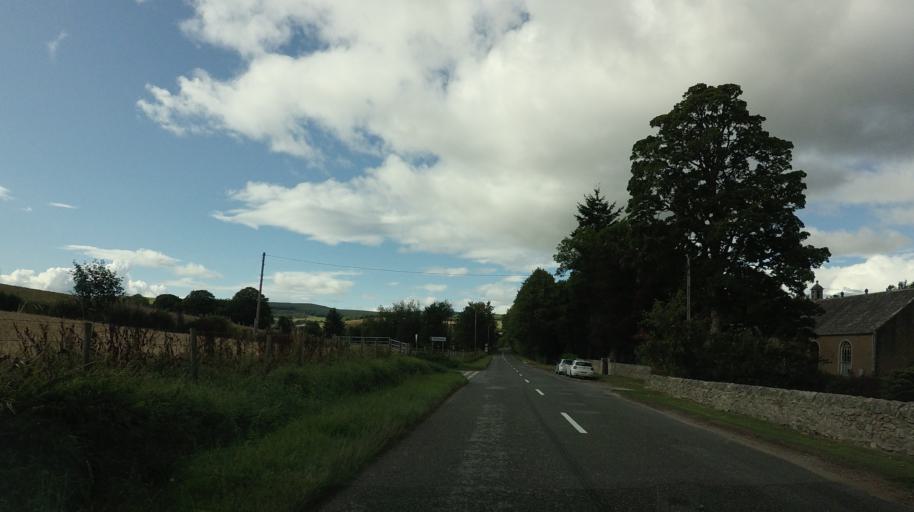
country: GB
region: Scotland
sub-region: Aberdeenshire
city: Alford
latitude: 57.2334
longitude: -2.7396
